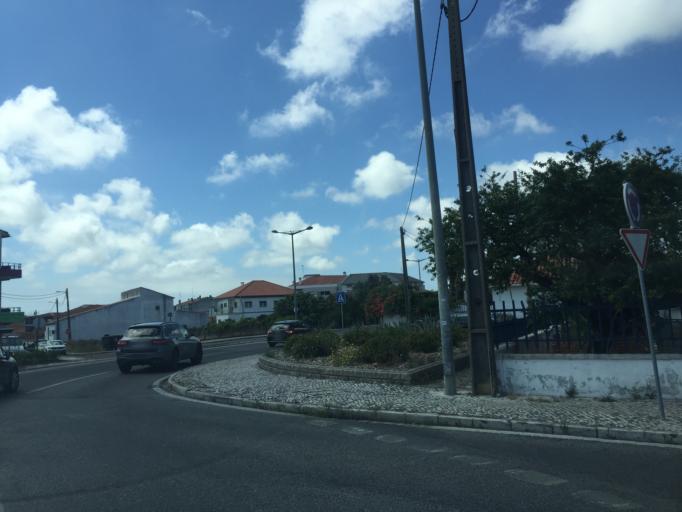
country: PT
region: Leiria
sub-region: Marinha Grande
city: Marinha Grande
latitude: 39.7408
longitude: -8.9346
